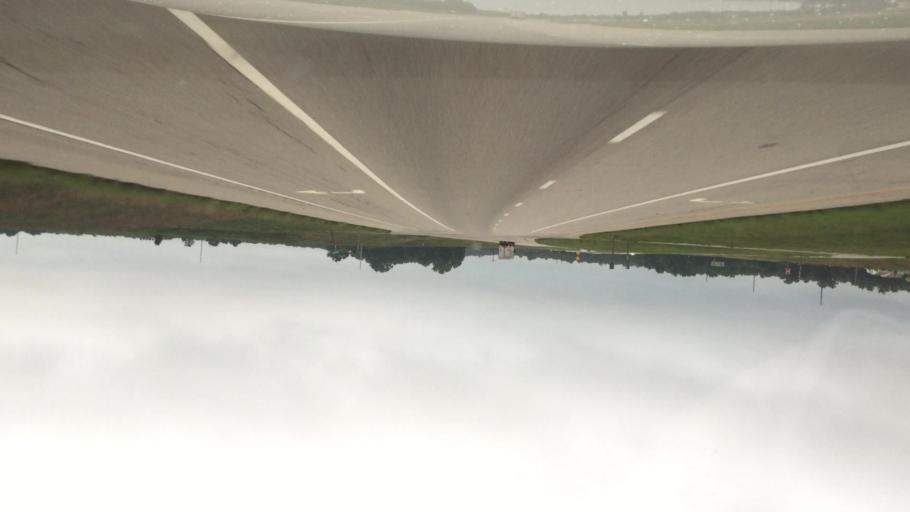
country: US
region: Kansas
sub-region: Montgomery County
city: Coffeyville
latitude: 37.0750
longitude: -95.5888
